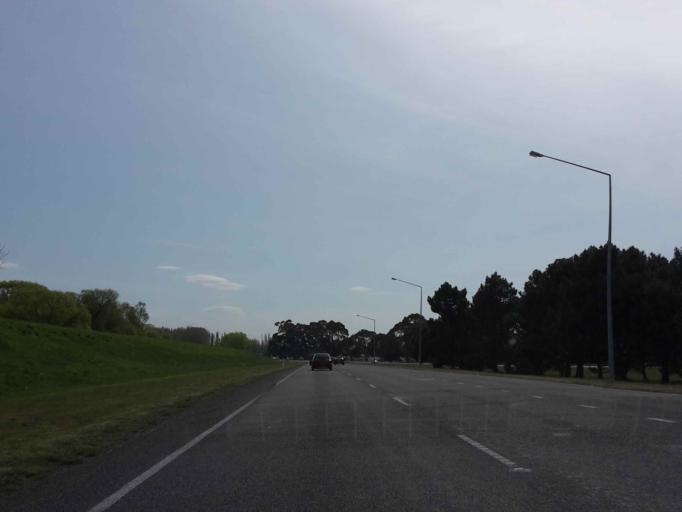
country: NZ
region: Canterbury
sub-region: Waimakariri District
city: Kaiapoi
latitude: -43.4274
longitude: 172.6468
